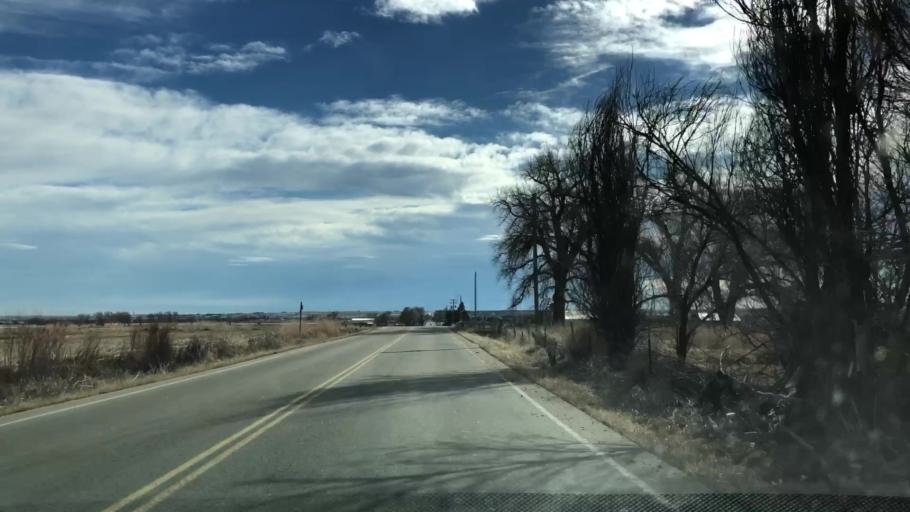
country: US
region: Colorado
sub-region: Weld County
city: Windsor
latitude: 40.5204
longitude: -104.9442
